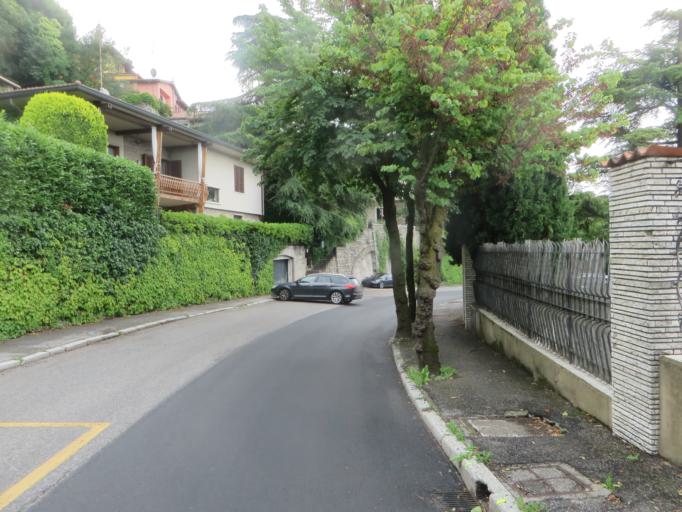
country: IT
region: Lombardy
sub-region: Provincia di Brescia
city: Brescia
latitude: 45.5392
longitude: 10.2383
